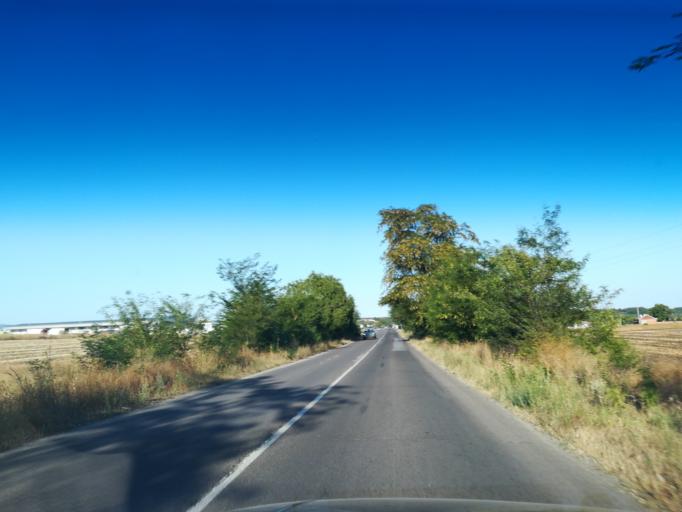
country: BG
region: Stara Zagora
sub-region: Obshtina Chirpan
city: Chirpan
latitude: 42.1750
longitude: 25.2005
